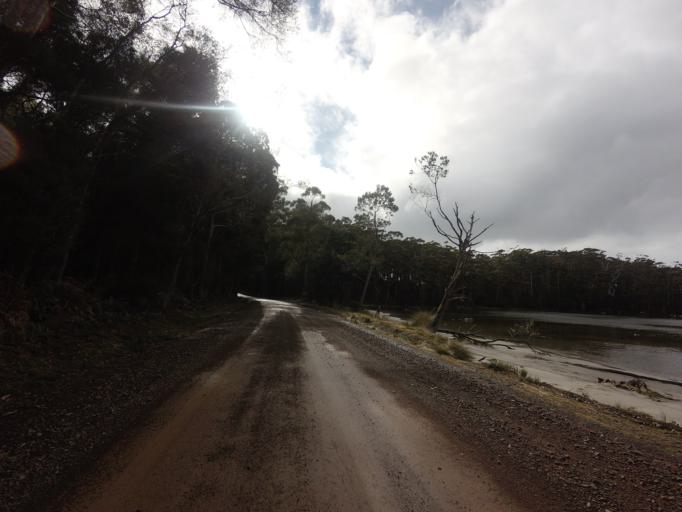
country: AU
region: Tasmania
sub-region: Huon Valley
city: Geeveston
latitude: -43.5656
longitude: 146.8875
